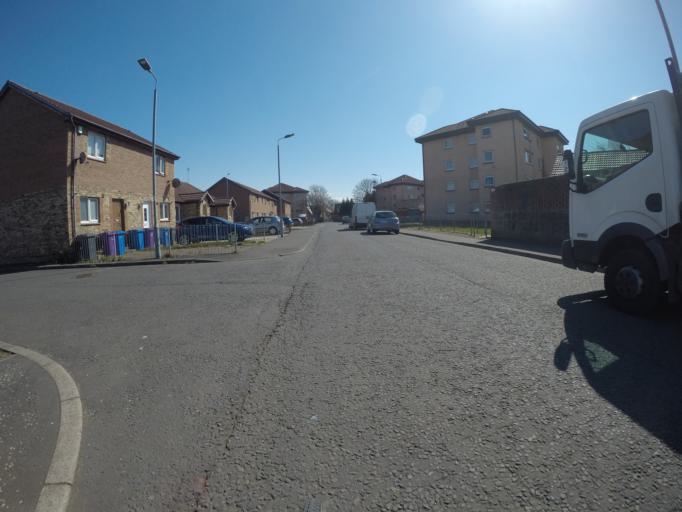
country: GB
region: Scotland
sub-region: North Ayrshire
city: Irvine
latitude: 55.6149
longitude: -4.6614
